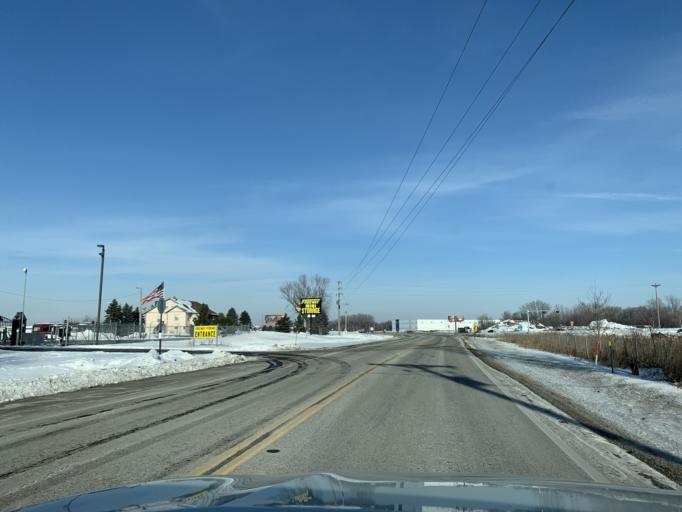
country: US
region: Minnesota
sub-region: Anoka County
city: Columbus
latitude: 45.2316
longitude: -93.0305
